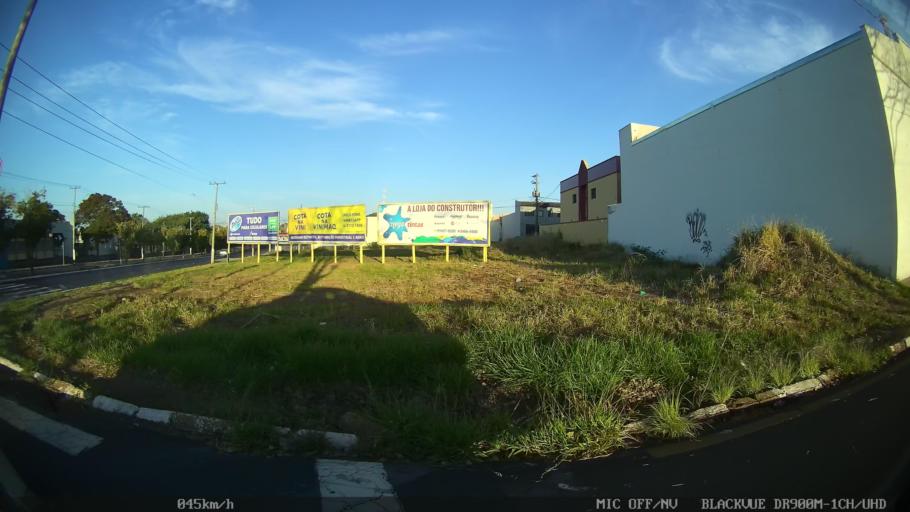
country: BR
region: Sao Paulo
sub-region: Franca
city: Franca
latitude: -20.5121
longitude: -47.3861
